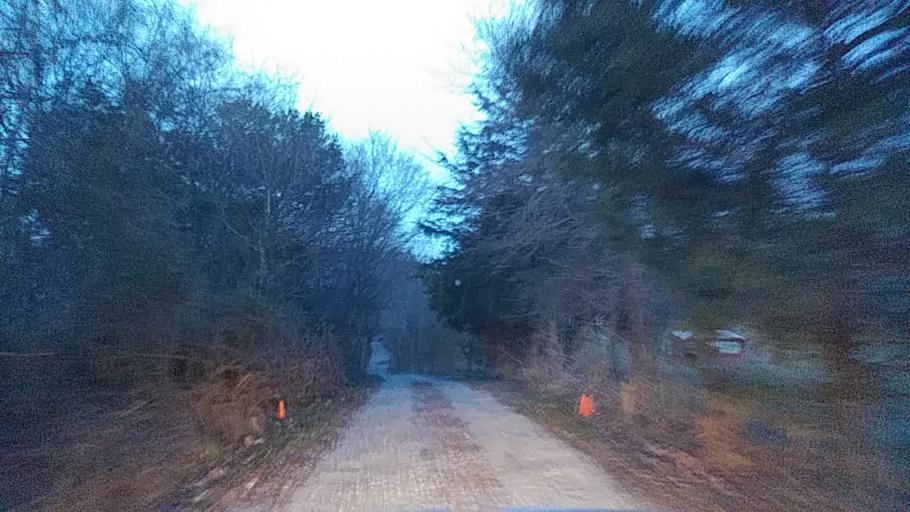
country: US
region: Tennessee
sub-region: Greene County
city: Mosheim
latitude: 36.0767
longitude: -82.9900
